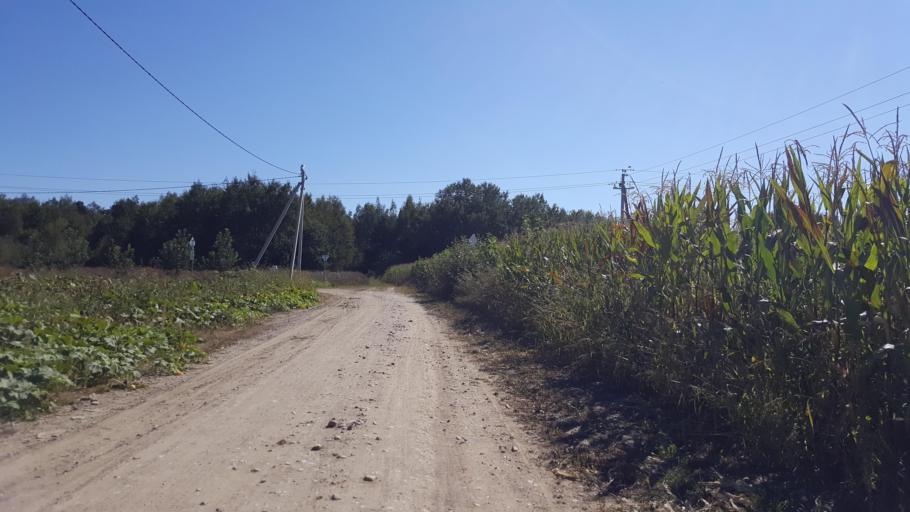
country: BY
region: Brest
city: Vysokaye
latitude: 52.2501
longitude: 23.5015
